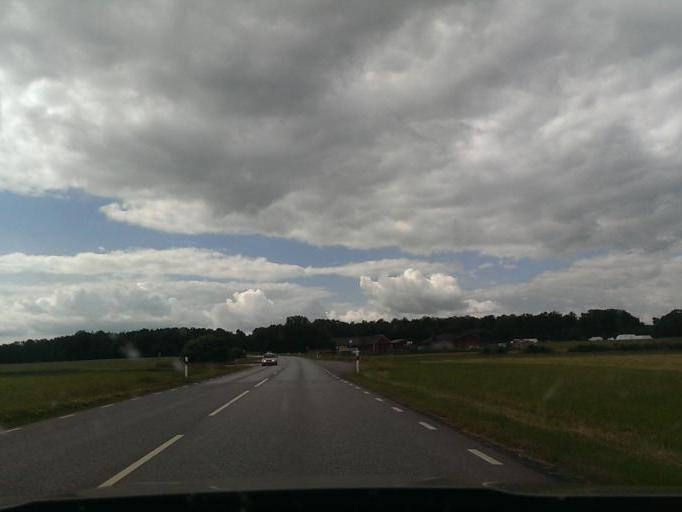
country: SE
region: Skane
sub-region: Eslovs Kommun
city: Stehag
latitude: 55.9339
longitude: 13.3805
